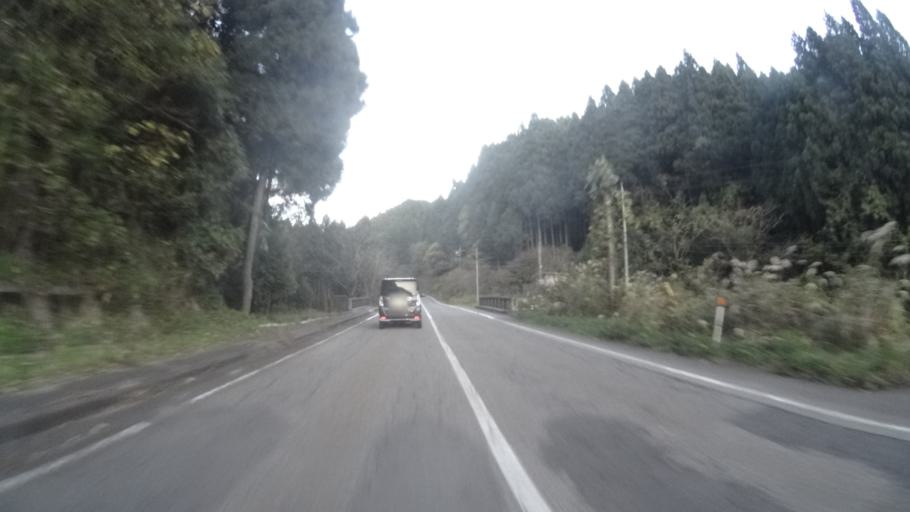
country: JP
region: Ishikawa
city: Nanao
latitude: 37.3183
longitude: 136.8074
